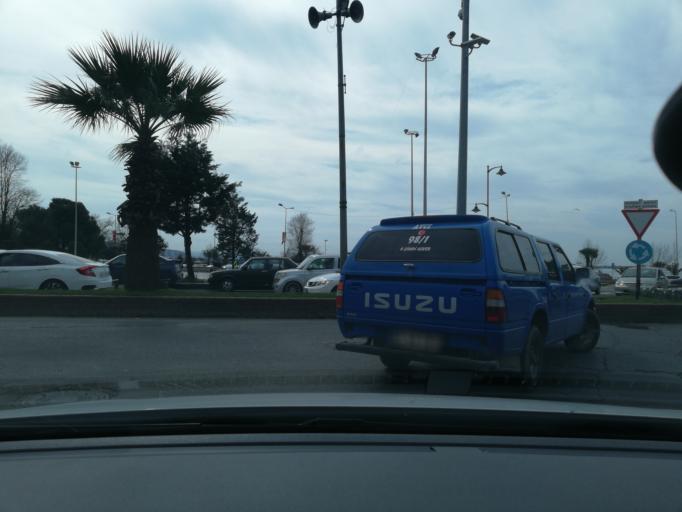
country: TR
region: Zonguldak
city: Eregli
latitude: 41.2798
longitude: 31.4209
